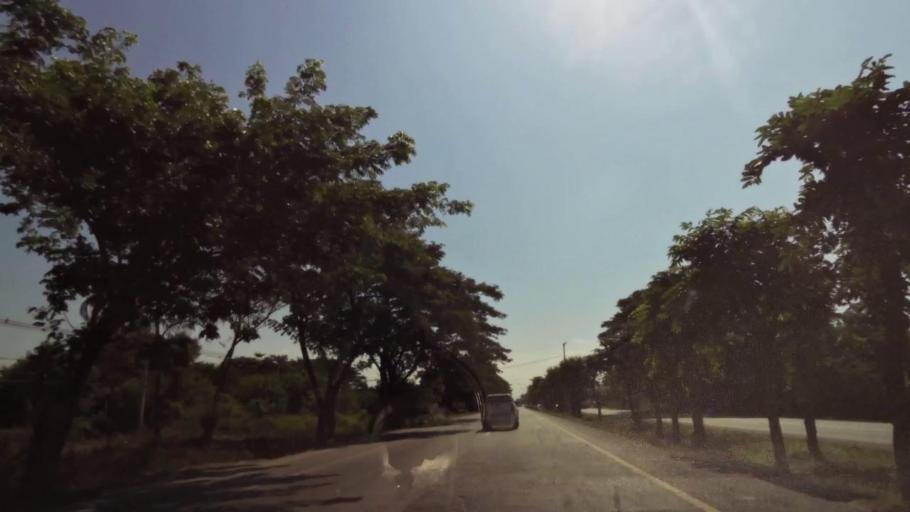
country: TH
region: Nakhon Sawan
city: Kao Liao
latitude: 15.7859
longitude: 100.1210
